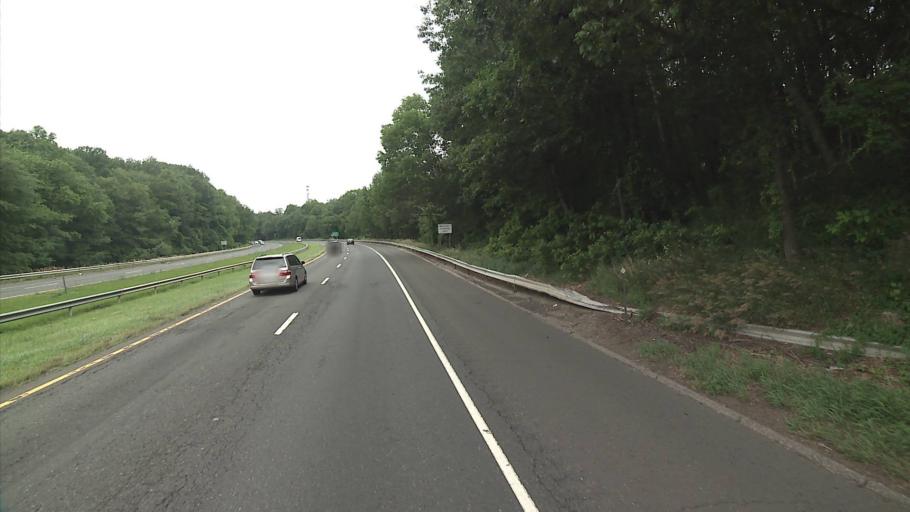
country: US
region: Connecticut
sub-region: Fairfield County
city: Newtown
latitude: 41.4242
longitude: -73.3692
